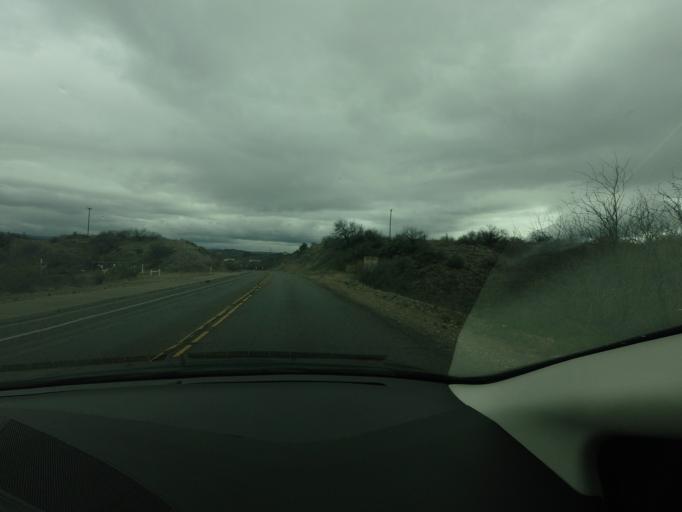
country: US
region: Arizona
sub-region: Yavapai County
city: Cottonwood
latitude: 34.7512
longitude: -112.0331
